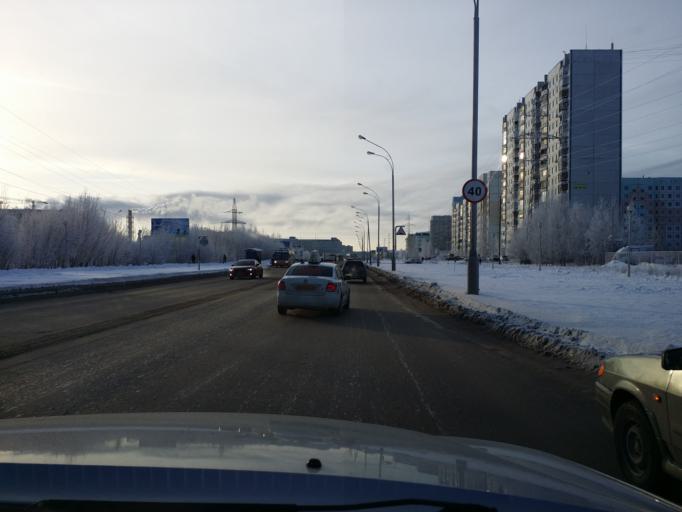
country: RU
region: Khanty-Mansiyskiy Avtonomnyy Okrug
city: Nizhnevartovsk
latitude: 60.9543
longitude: 76.5748
